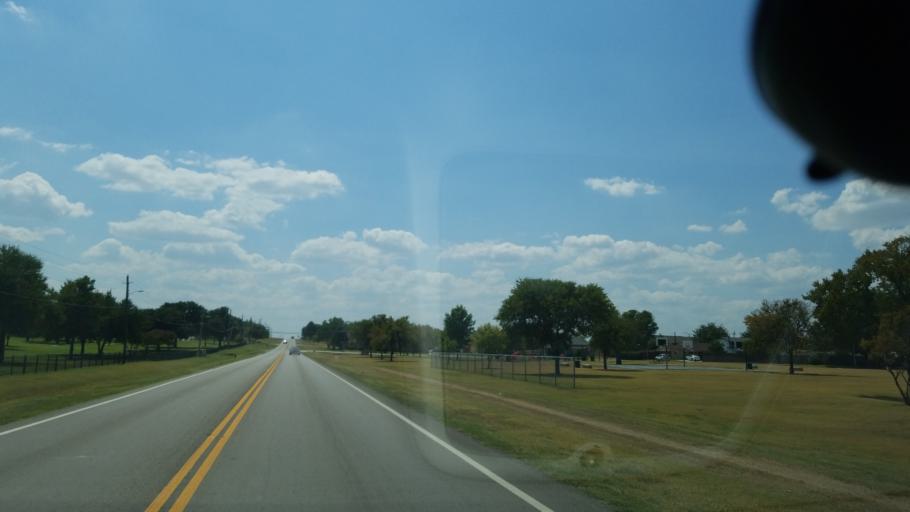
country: US
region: Texas
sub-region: Dallas County
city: Grand Prairie
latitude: 32.7007
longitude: -96.9855
